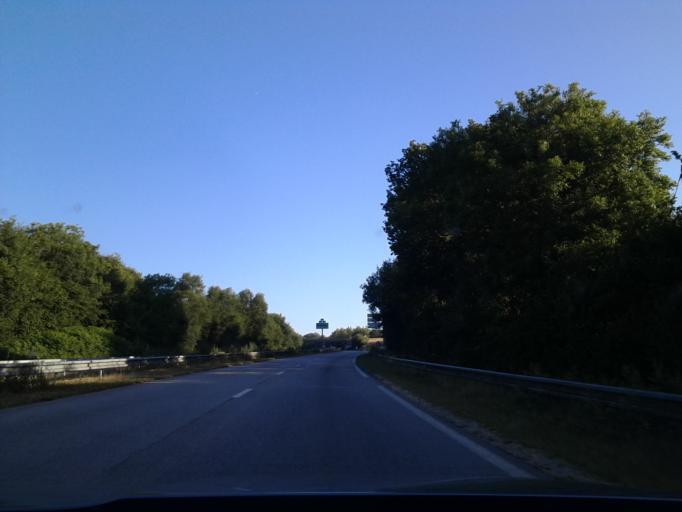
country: FR
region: Lower Normandy
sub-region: Departement de la Manche
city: Brix
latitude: 49.5606
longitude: -1.5671
